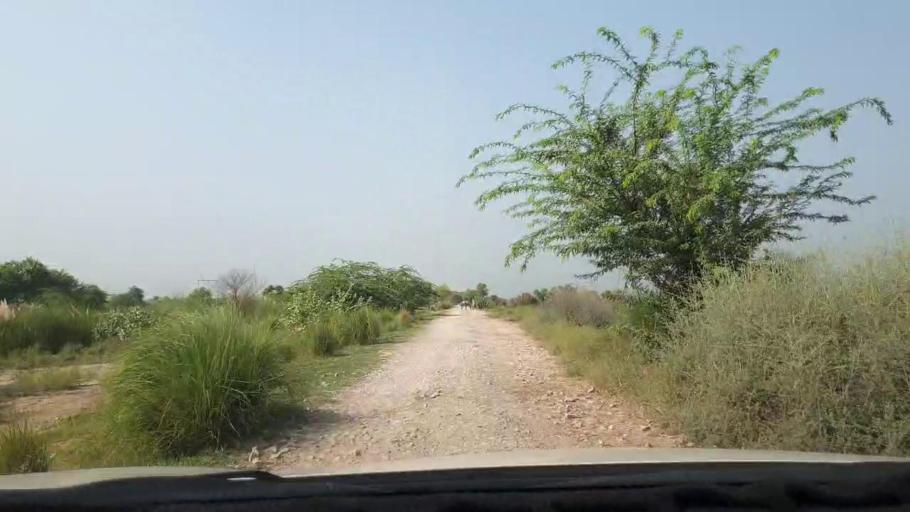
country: PK
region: Sindh
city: Goth Garelo
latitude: 27.4577
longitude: 68.1255
